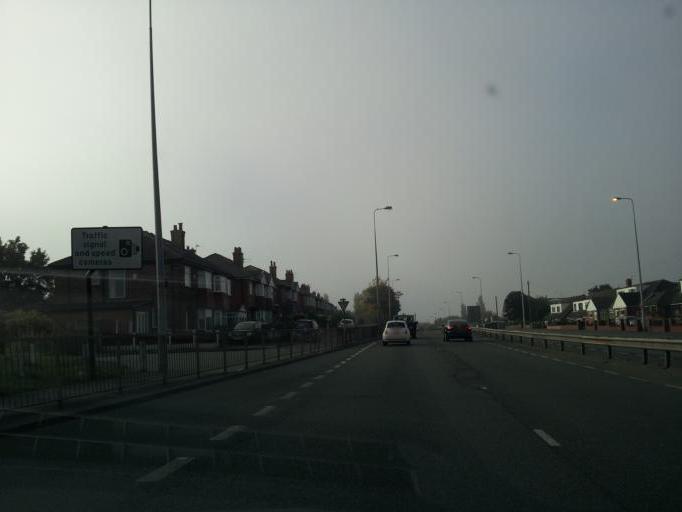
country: GB
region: England
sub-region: Borough of Oldham
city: Royton
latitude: 53.5540
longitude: -2.1409
